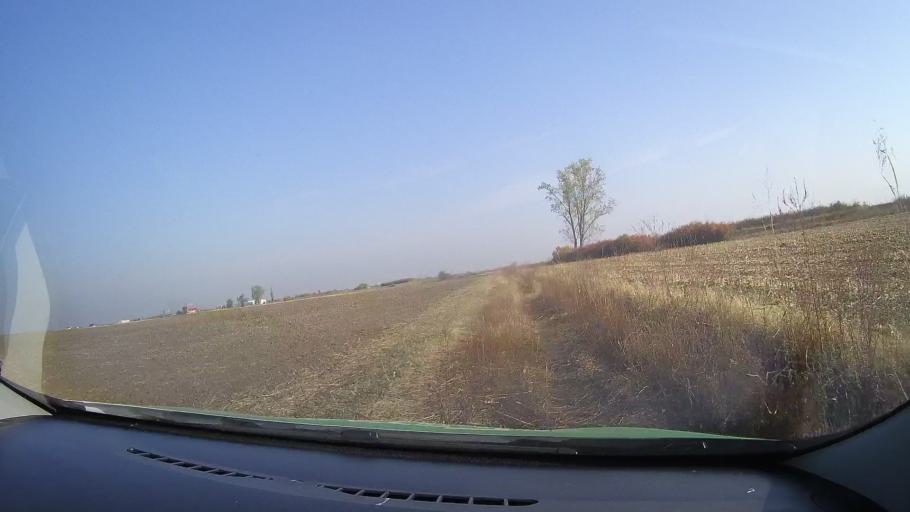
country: RO
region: Arad
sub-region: Comuna Pilu
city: Pilu
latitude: 46.5607
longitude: 21.3460
